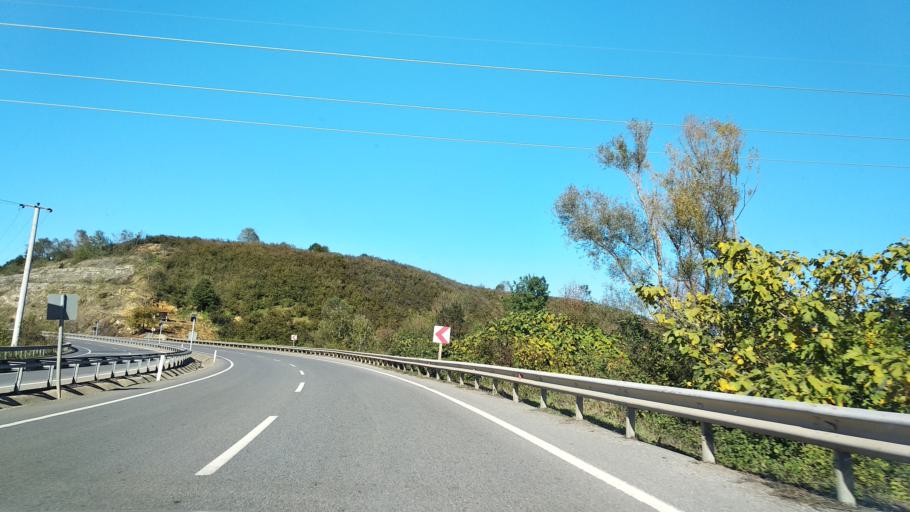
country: TR
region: Sakarya
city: Karasu
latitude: 41.0827
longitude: 30.6478
